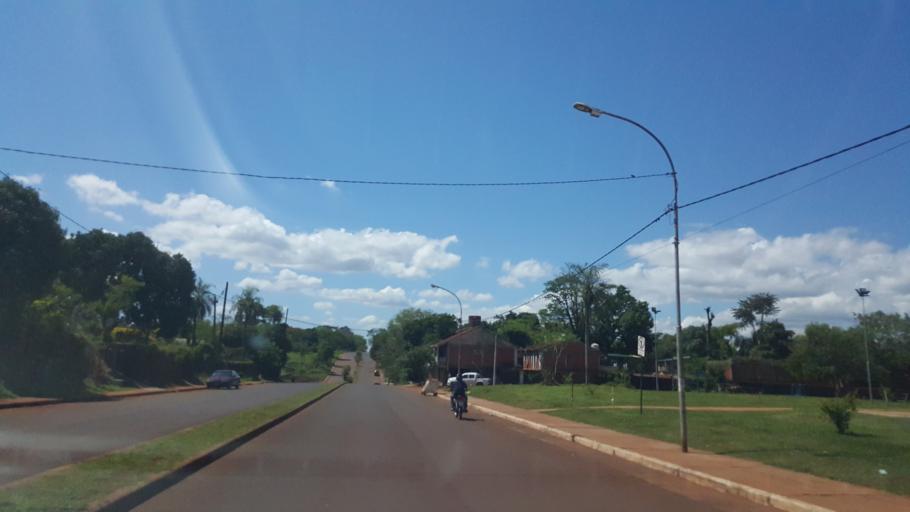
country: AR
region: Misiones
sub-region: Departamento de Capital
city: Posadas
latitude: -27.3647
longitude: -55.9389
